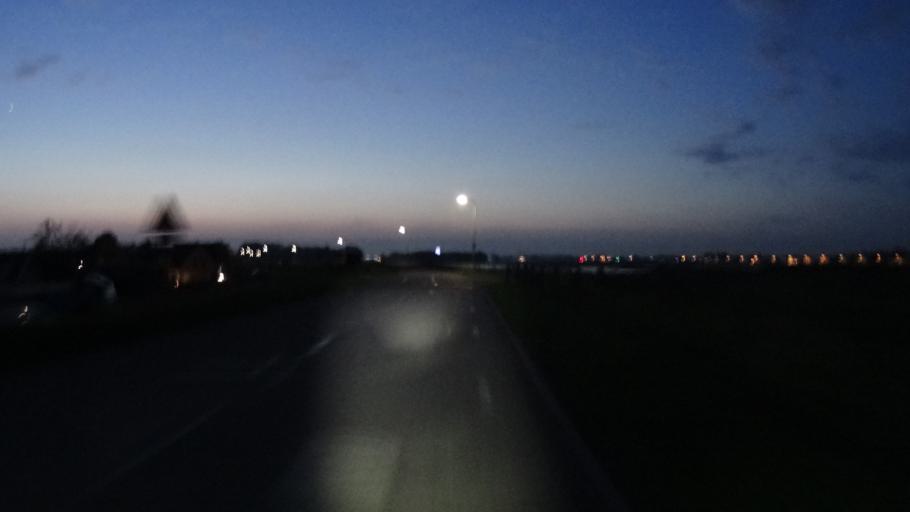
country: NL
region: South Holland
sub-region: Gemeente Hendrik-Ido-Ambacht
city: Hendrik-Ido-Ambacht
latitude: 51.8600
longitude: 4.6395
